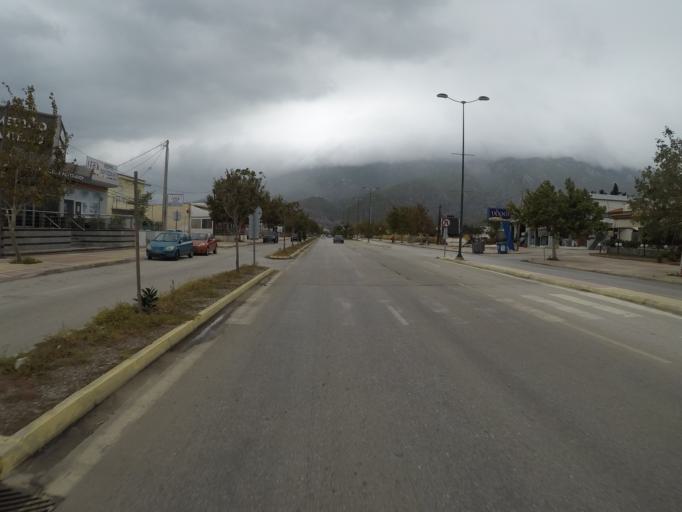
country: GR
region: Peloponnese
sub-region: Nomos Korinthias
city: Loutraki
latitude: 37.9613
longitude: 22.9788
